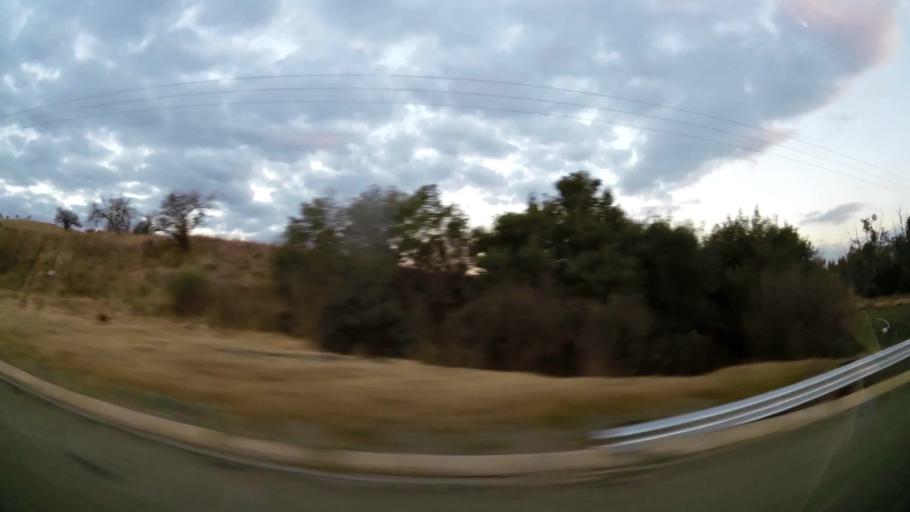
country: ZA
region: Gauteng
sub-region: West Rand District Municipality
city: Krugersdorp
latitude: -26.0393
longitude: 27.7215
